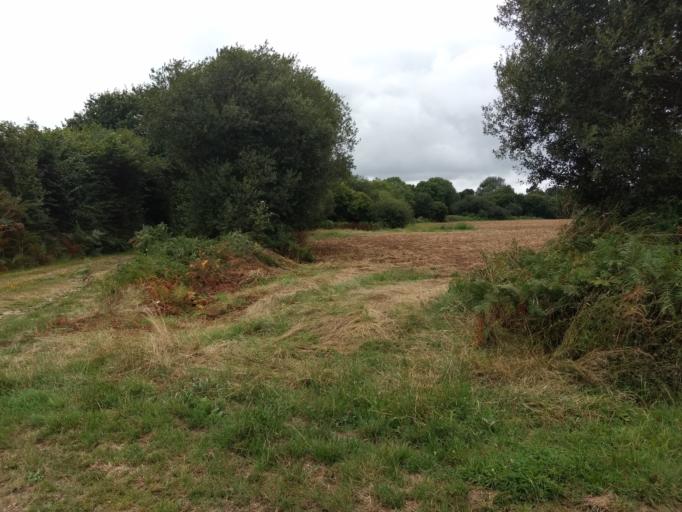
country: FR
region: Brittany
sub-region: Departement du Finistere
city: Loperhet
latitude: 48.3670
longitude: -4.2919
